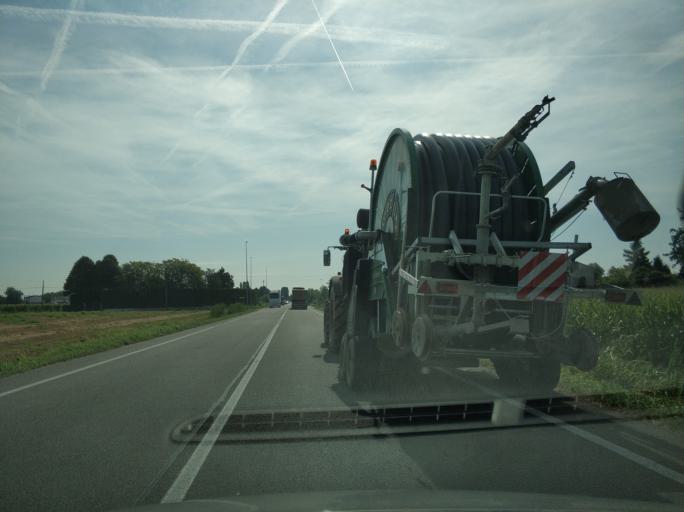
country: IT
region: Veneto
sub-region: Provincia di Padova
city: Arre
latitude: 45.2113
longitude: 11.9313
